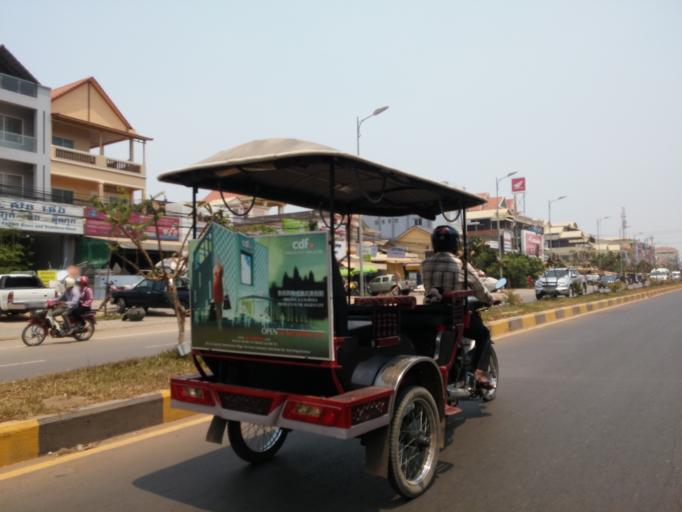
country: KH
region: Siem Reap
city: Siem Reap
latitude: 13.3608
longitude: 103.8713
